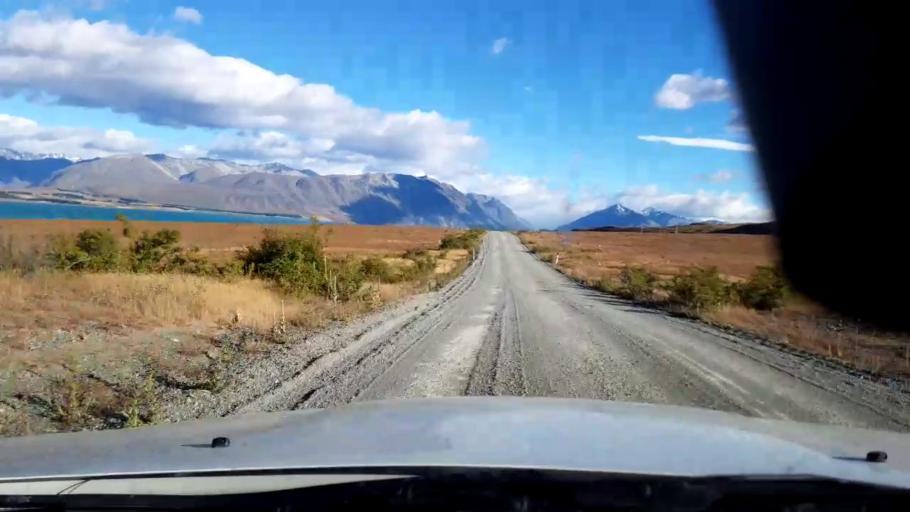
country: NZ
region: Canterbury
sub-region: Timaru District
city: Pleasant Point
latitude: -43.9200
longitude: 170.5594
